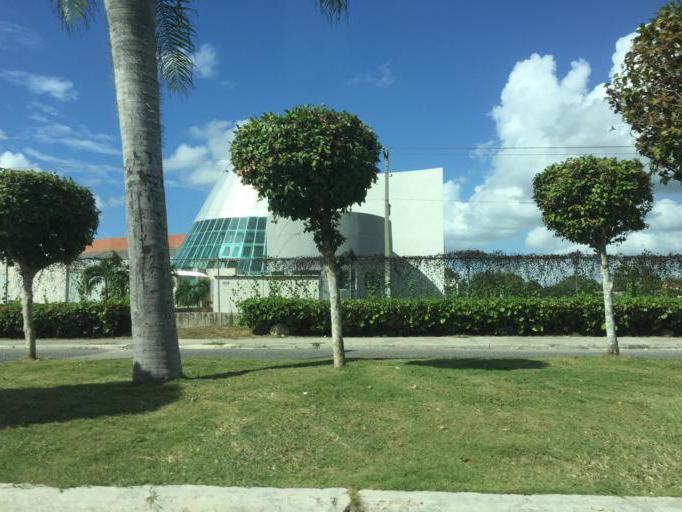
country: DO
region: Santo Domingo
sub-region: Santo Domingo
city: Boca Chica
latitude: 18.4506
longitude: -69.6638
